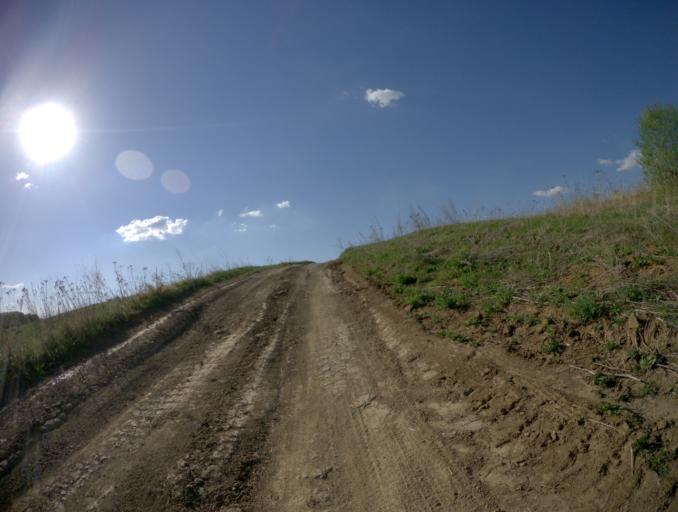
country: RU
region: Ivanovo
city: Gavrilov Posad
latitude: 56.3410
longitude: 40.2110
